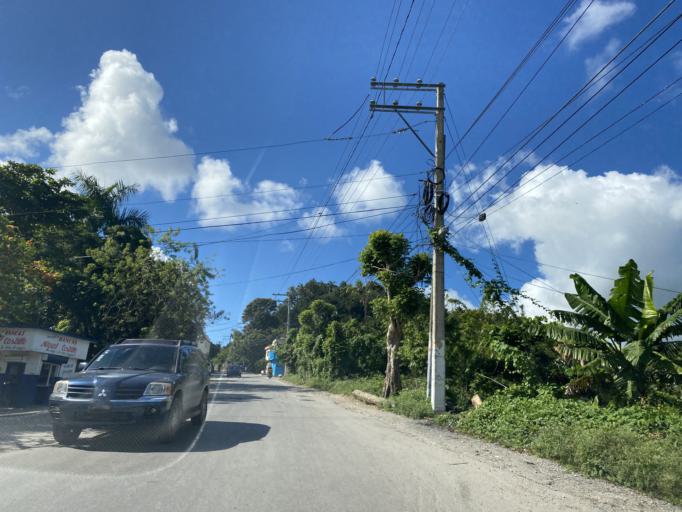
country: DO
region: Samana
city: Samana
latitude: 19.2069
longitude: -69.3493
